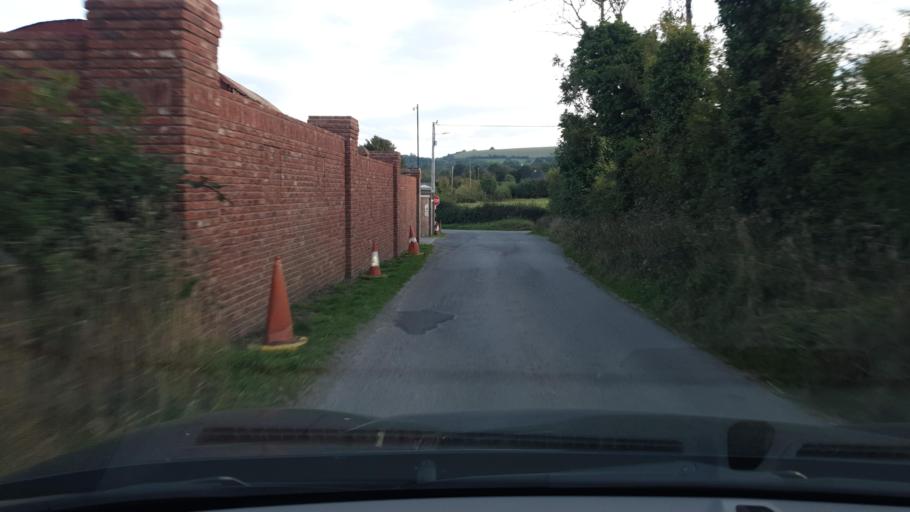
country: IE
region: Leinster
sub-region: An Mhi
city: Stamullin
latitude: 53.5881
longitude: -6.2456
